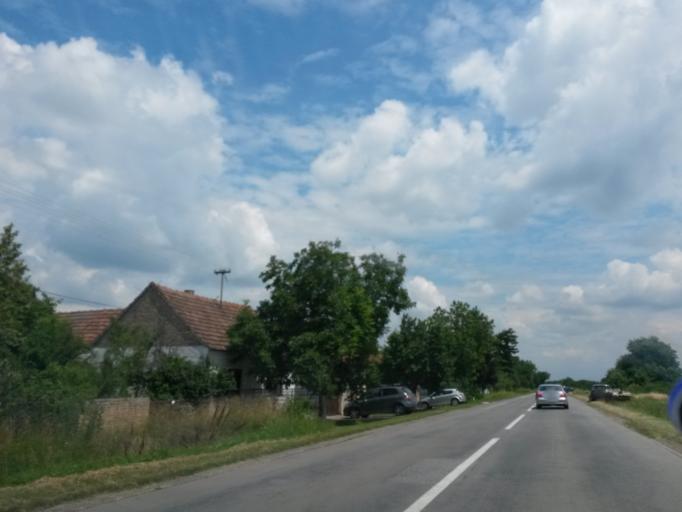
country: HR
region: Osjecko-Baranjska
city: Dalj
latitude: 45.5080
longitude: 19.0558
